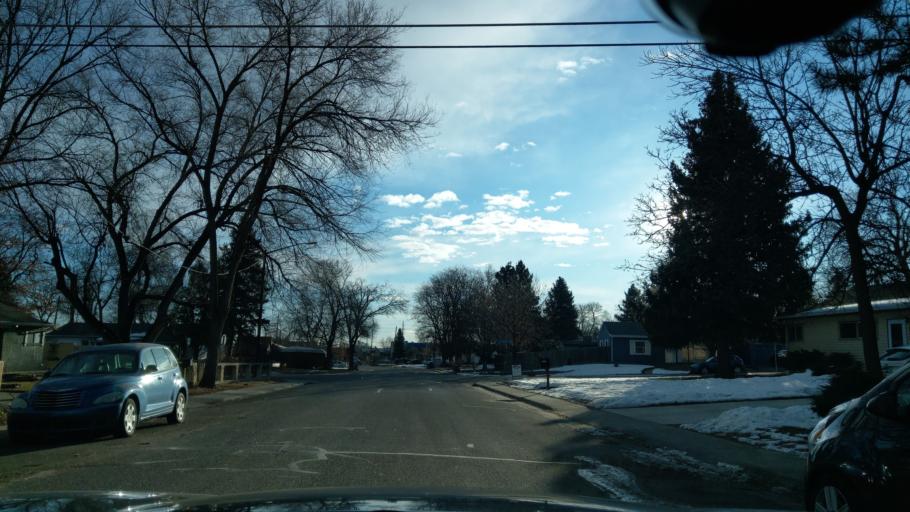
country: US
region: Colorado
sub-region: Jefferson County
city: Lakewood
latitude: 39.7305
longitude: -105.1120
